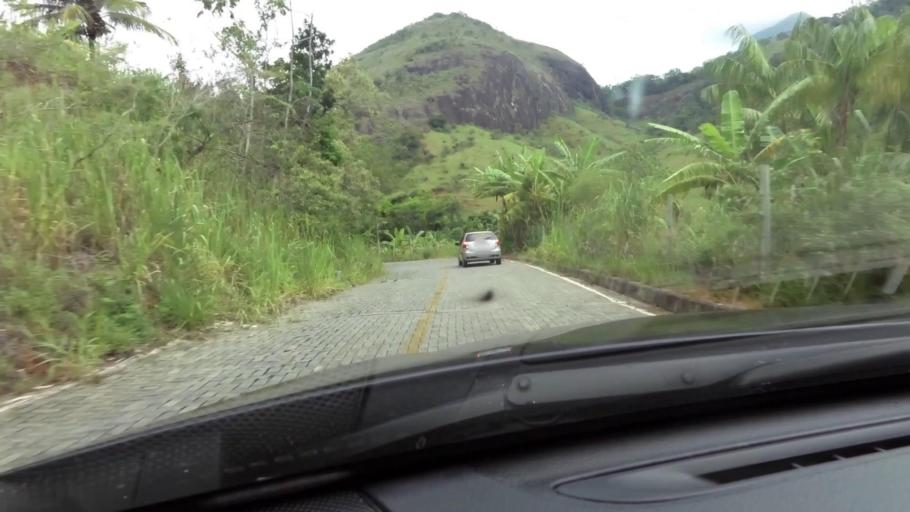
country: BR
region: Espirito Santo
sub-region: Guarapari
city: Guarapari
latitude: -20.6066
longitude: -40.5364
